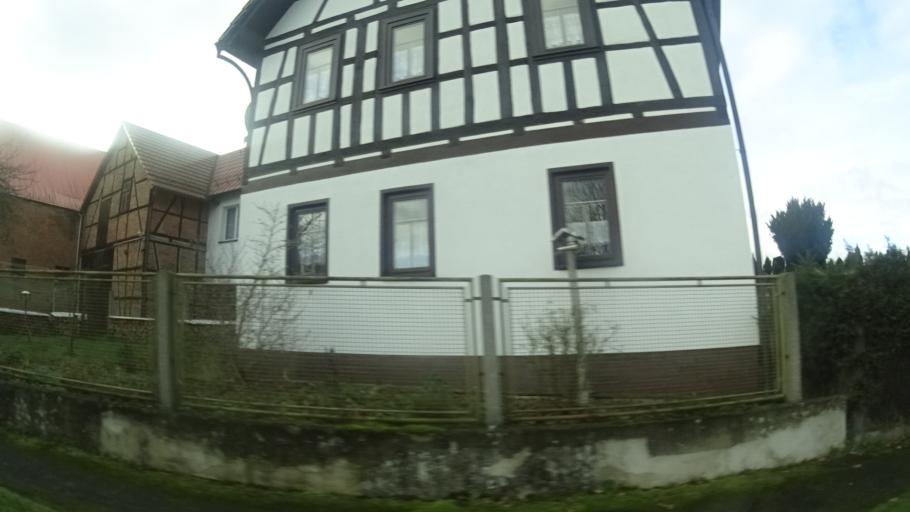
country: DE
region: Thuringia
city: Allendorf
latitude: 50.6563
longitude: 11.1575
